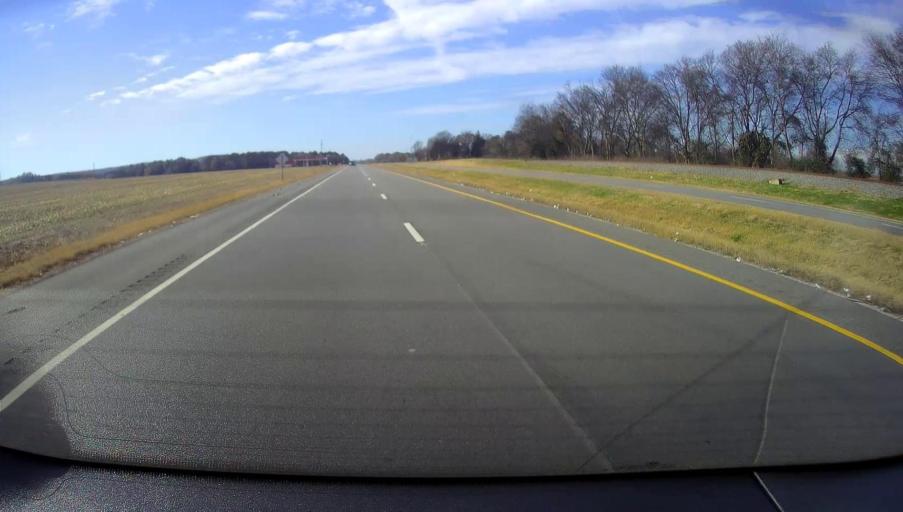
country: US
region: Alabama
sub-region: Colbert County
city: Cherokee
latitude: 34.7598
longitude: -88.0029
